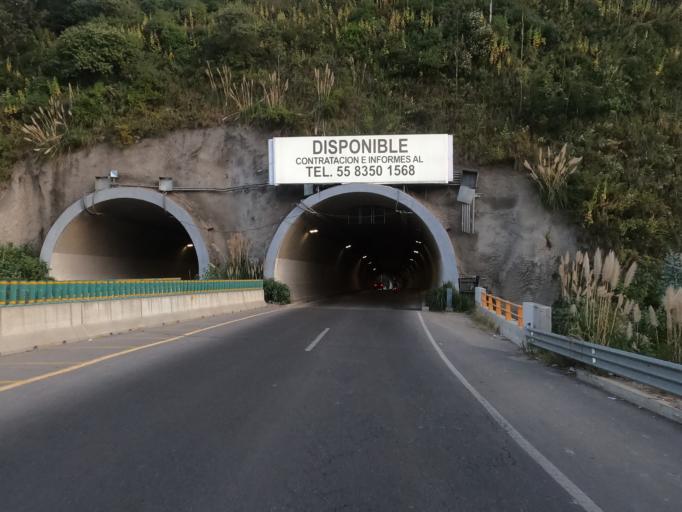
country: MX
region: Mexico
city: San Bartolome Coatepec
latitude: 19.4121
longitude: -99.2837
